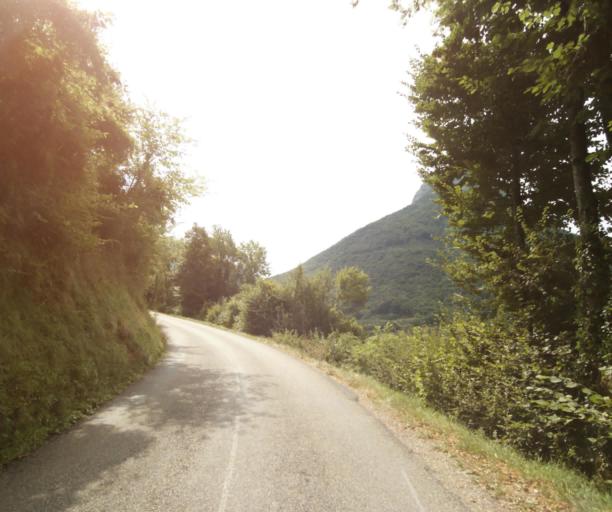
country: FR
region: Rhone-Alpes
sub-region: Departement de l'Isere
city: Saint-Egreve
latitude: 45.2541
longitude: 5.7135
